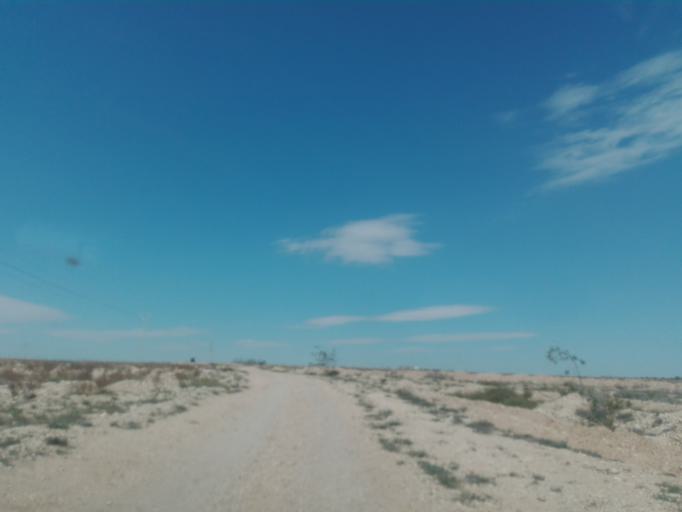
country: TN
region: Safaqis
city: Sfax
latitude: 34.6874
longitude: 10.5440
